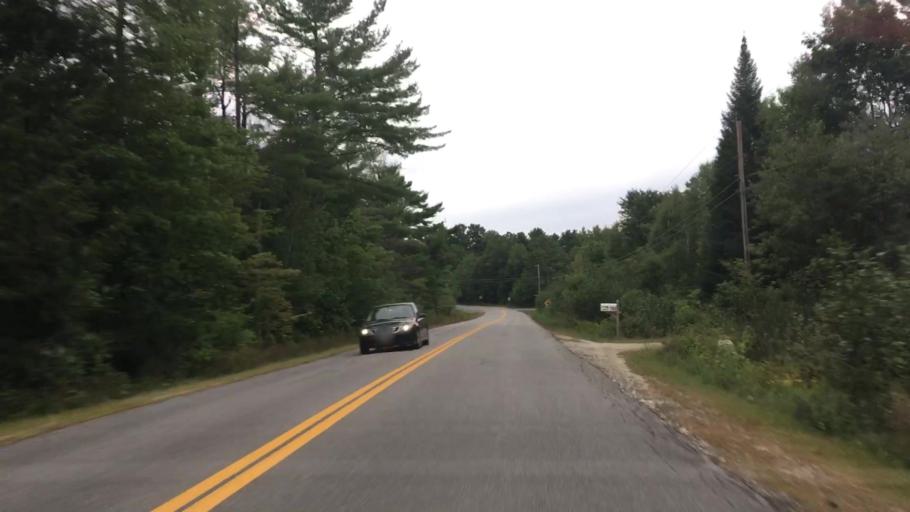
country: US
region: Maine
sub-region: Cumberland County
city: New Gloucester
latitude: 43.9028
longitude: -70.2079
